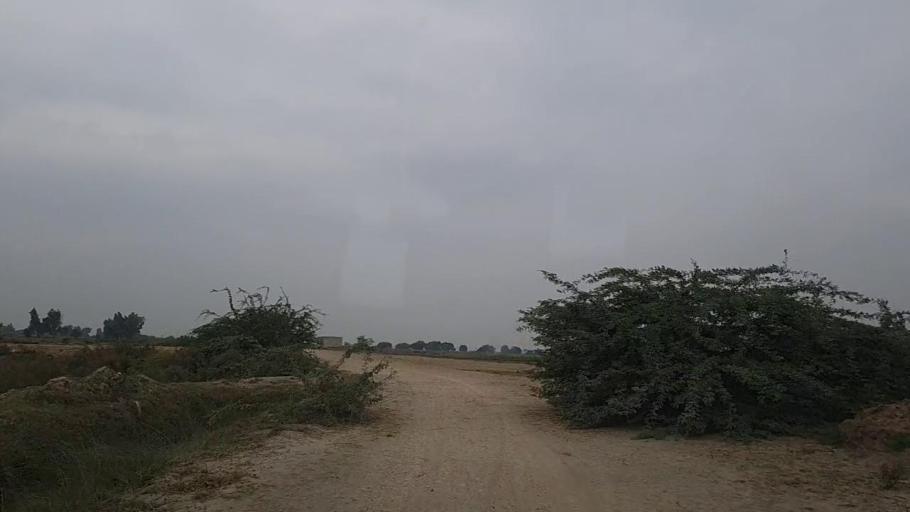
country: PK
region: Sindh
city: Mirpur Sakro
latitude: 24.6149
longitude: 67.7176
